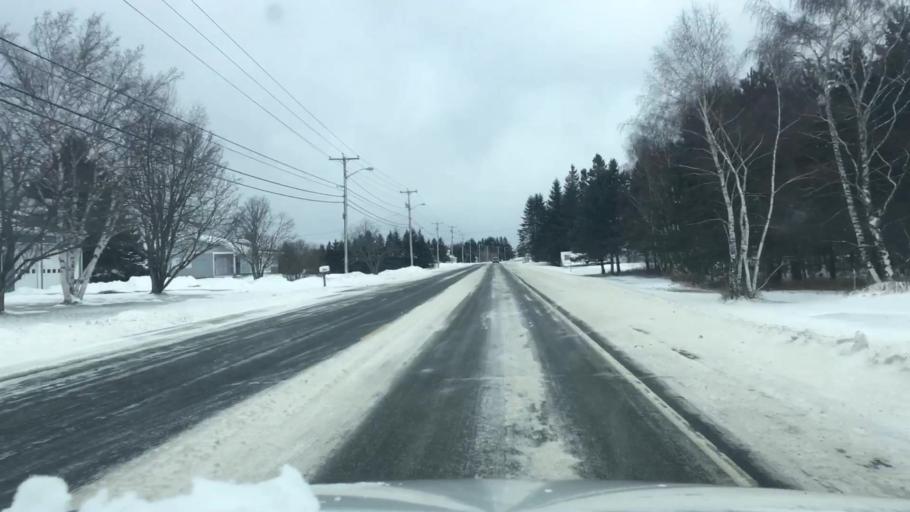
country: US
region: Maine
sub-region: Aroostook County
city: Madawaska
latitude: 47.3455
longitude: -68.2540
